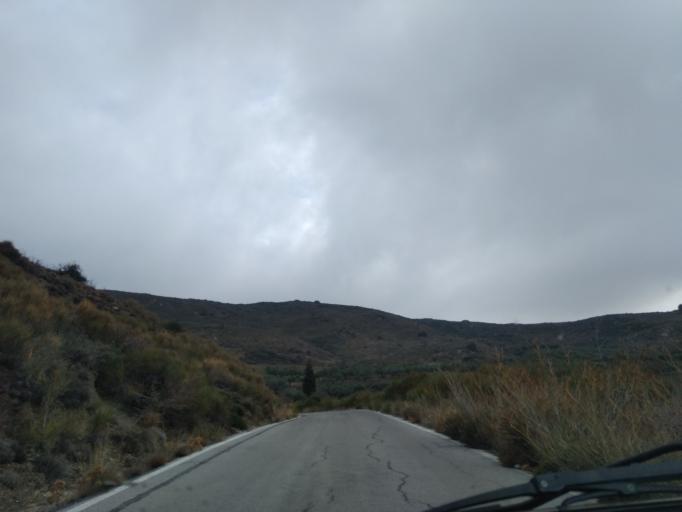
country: GR
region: Crete
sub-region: Nomos Lasithiou
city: Siteia
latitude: 35.1439
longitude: 26.0238
